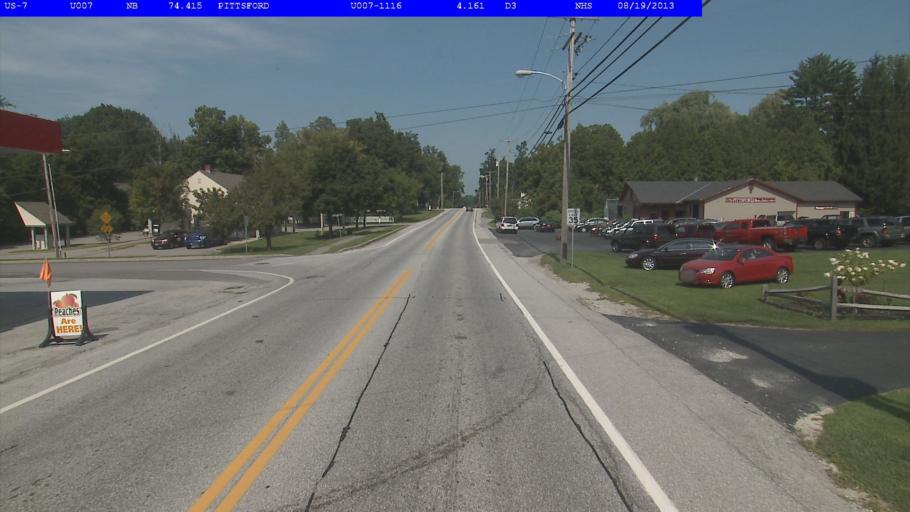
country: US
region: Vermont
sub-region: Rutland County
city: Brandon
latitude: 43.7087
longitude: -73.0303
